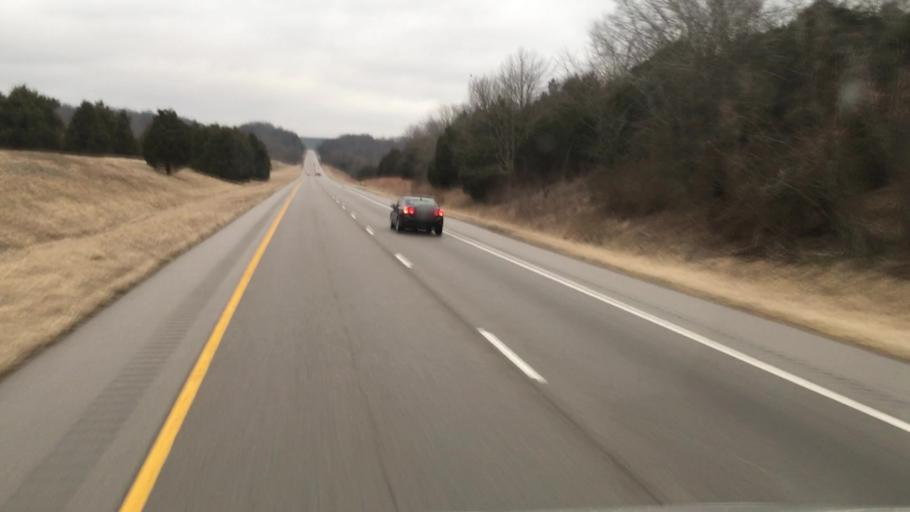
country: US
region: Illinois
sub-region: Johnson County
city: Vienna
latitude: 37.4687
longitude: -88.8910
